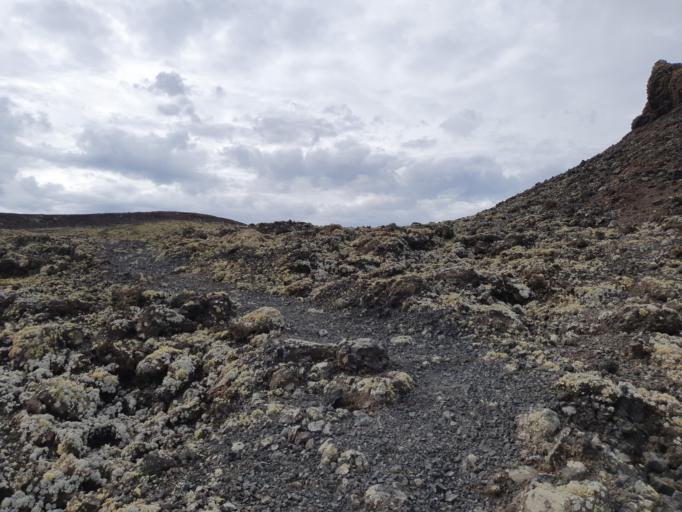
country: ES
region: Canary Islands
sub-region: Provincia de Las Palmas
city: Tinajo
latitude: 29.0223
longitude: -13.7113
